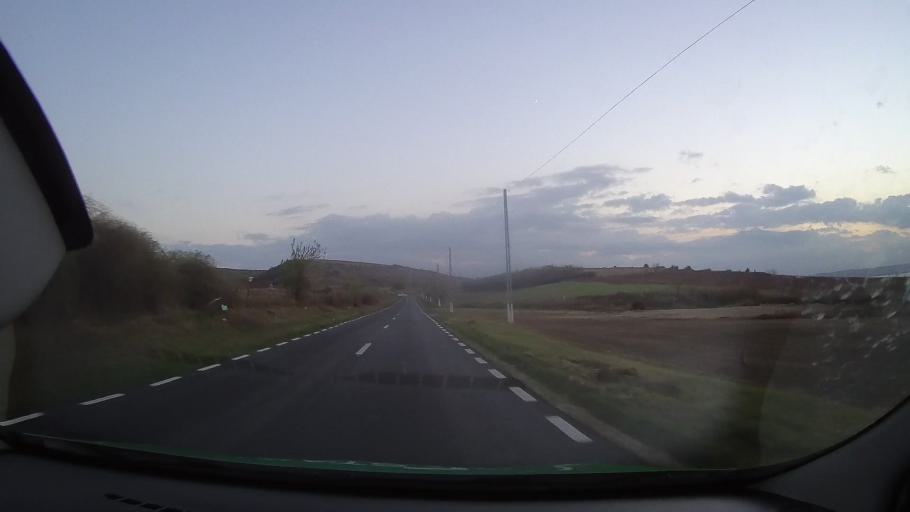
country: RO
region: Constanta
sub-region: Comuna Oltina
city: Oltina
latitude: 44.1542
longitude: 27.6675
